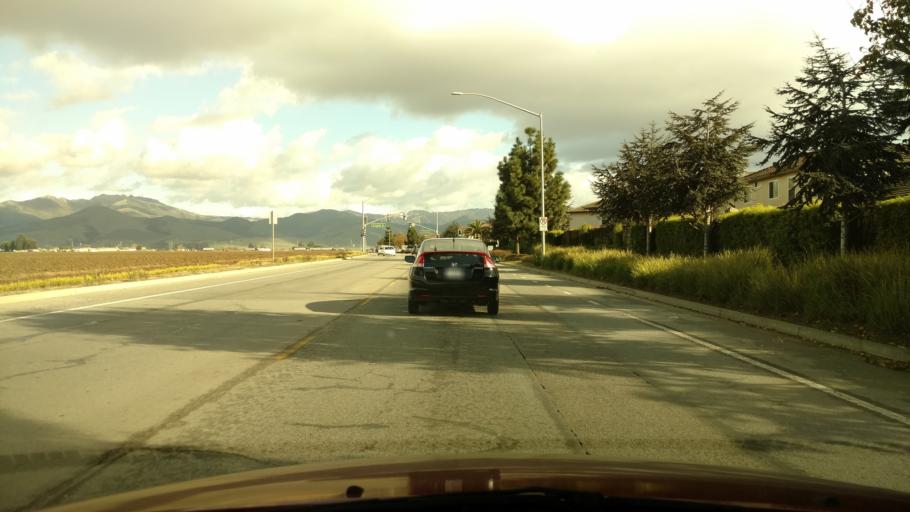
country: US
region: California
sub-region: Monterey County
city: Salinas
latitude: 36.7158
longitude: -121.6350
